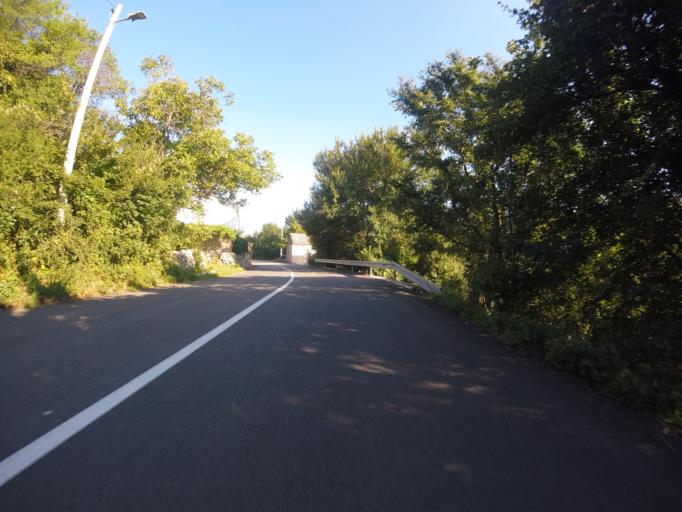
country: HR
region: Primorsko-Goranska
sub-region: Grad Crikvenica
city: Jadranovo
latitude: 45.2522
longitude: 14.6248
